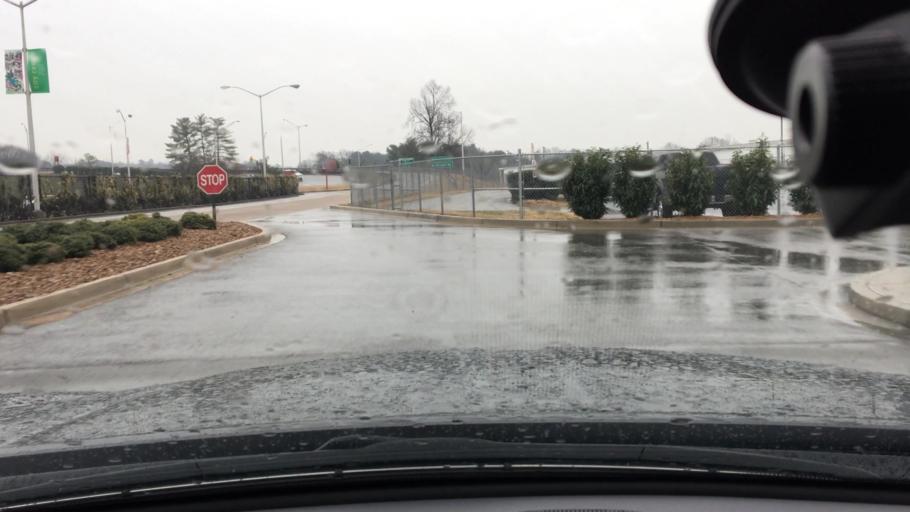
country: US
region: Tennessee
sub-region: Hamilton County
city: East Ridge
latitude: 35.0354
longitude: -85.1962
